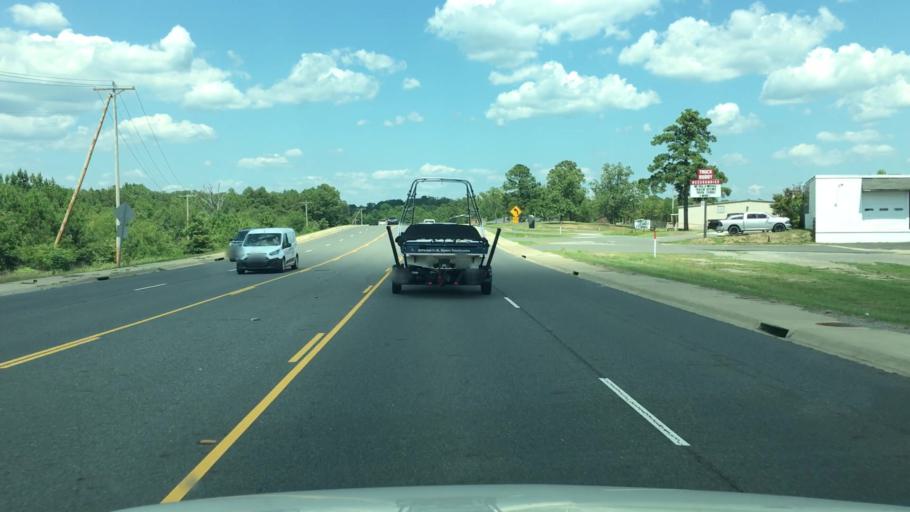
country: US
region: Arkansas
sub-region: Garland County
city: Lake Hamilton
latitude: 34.4511
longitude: -93.0821
